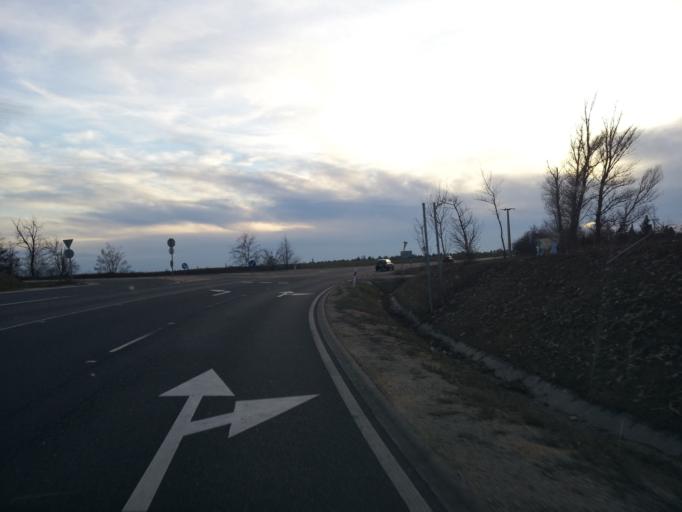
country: HU
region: Fejer
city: Lepseny
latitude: 47.0179
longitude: 18.1843
